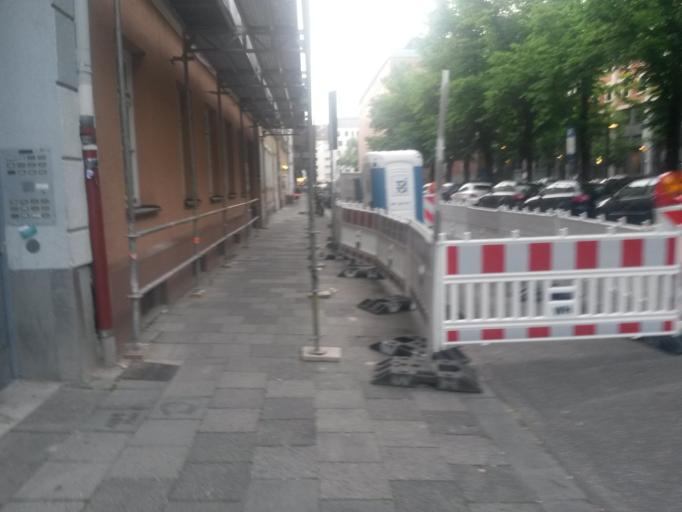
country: DE
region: Bavaria
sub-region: Upper Bavaria
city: Munich
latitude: 48.1317
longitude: 11.5821
